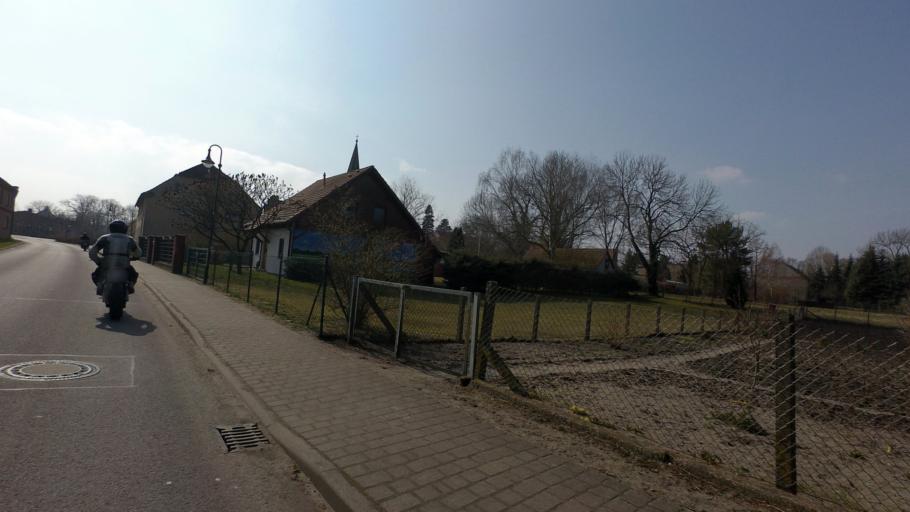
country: DE
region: Brandenburg
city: Gross Kreutz
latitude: 52.4042
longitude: 12.8255
